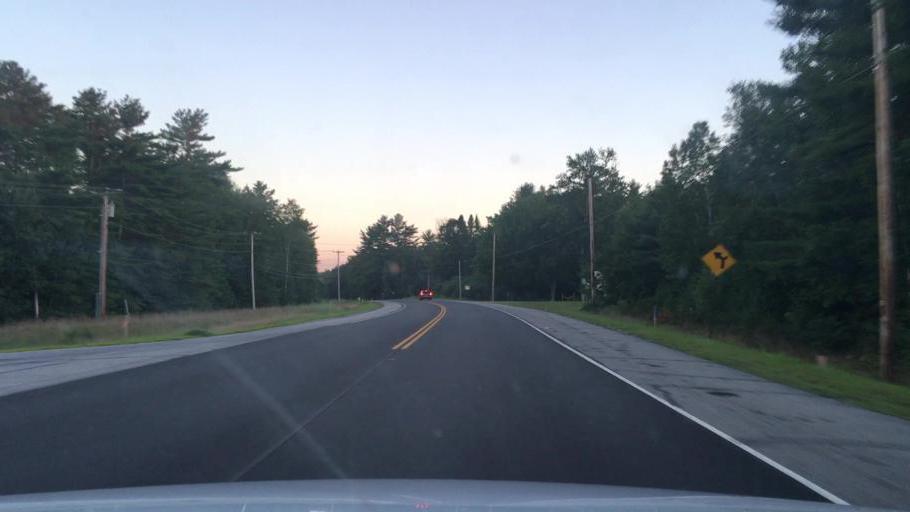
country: US
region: Maine
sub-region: Androscoggin County
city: Turner
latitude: 44.2451
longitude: -70.2604
